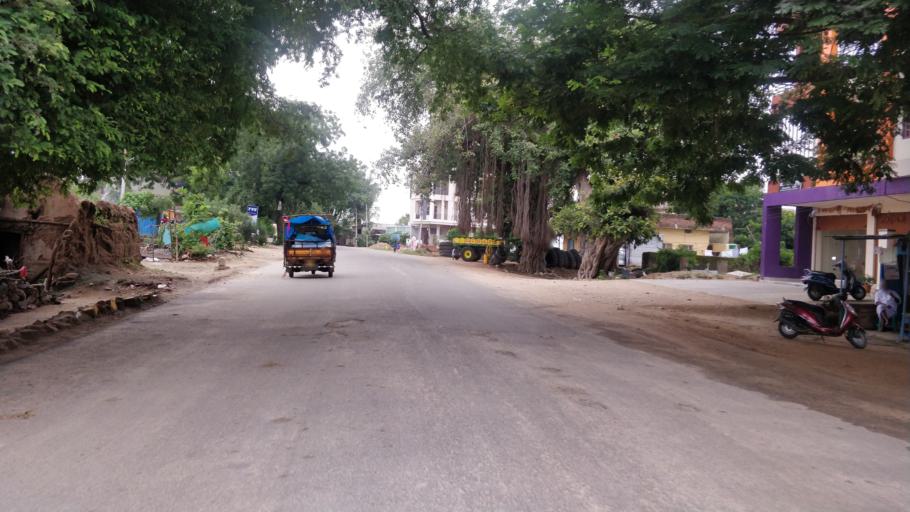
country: IN
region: Telangana
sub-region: Medak
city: Narsingi
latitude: 18.1844
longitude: 78.3975
